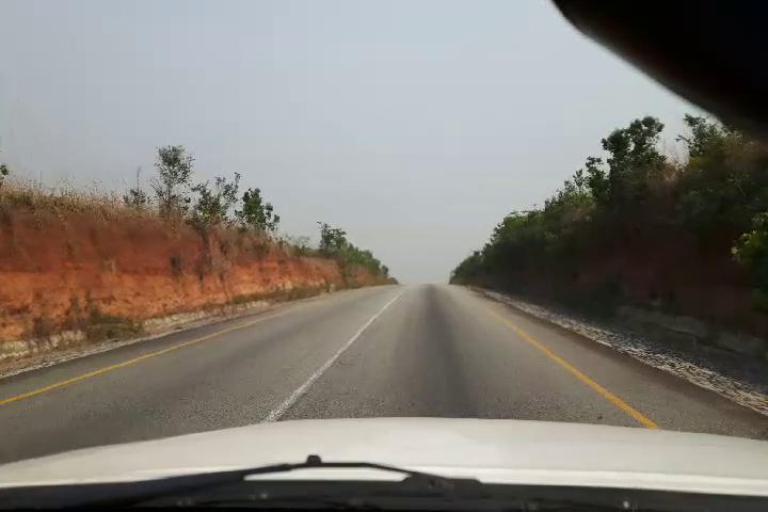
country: SL
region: Southern Province
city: Largo
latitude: 8.2287
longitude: -12.0783
